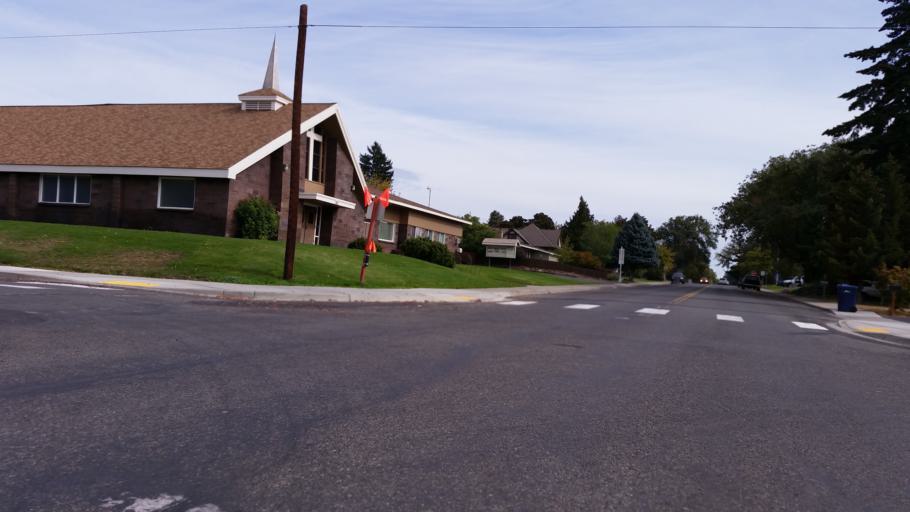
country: US
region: Washington
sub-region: Kittitas County
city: Ellensburg
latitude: 46.9915
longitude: -120.5391
